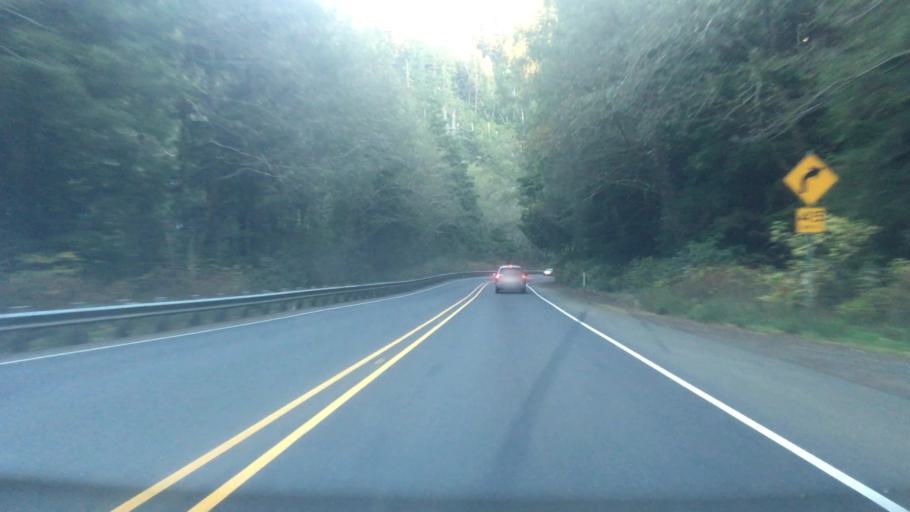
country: US
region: Oregon
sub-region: Clatsop County
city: Cannon Beach
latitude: 45.7749
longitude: -123.9450
